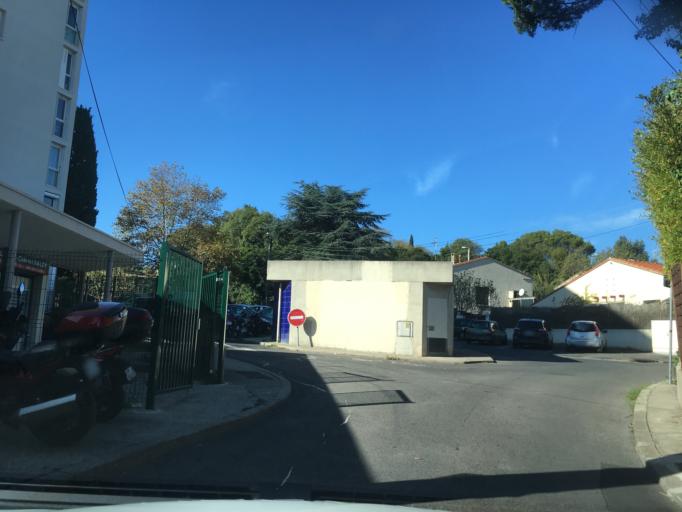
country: FR
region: Languedoc-Roussillon
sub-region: Departement de l'Herault
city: Montpellier
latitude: 43.6061
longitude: 3.8483
